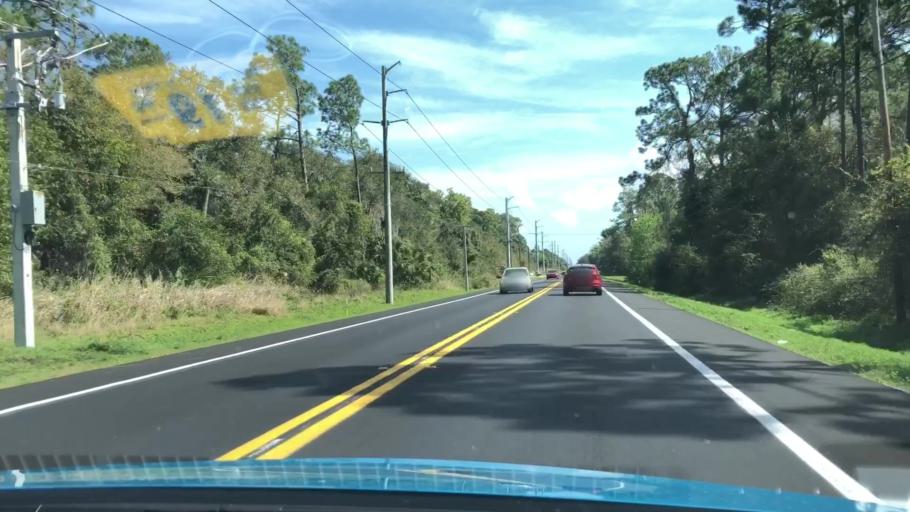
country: US
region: Florida
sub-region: Brevard County
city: Mims
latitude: 28.6659
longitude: -80.8942
